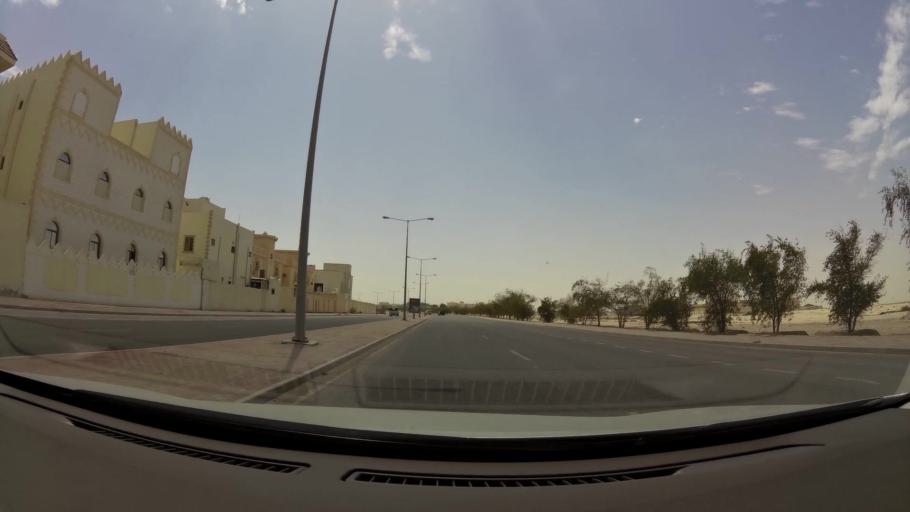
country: QA
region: Baladiyat ar Rayyan
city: Ar Rayyan
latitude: 25.2981
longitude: 51.4074
